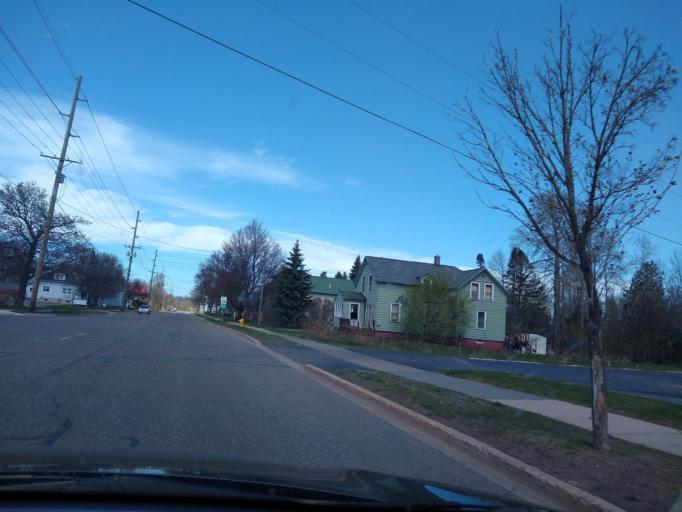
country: US
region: Michigan
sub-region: Marquette County
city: Marquette
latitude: 46.5673
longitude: -87.3959
